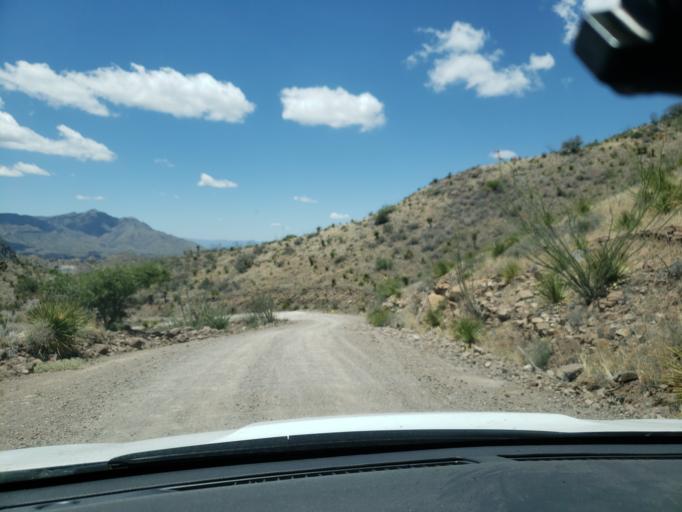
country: MX
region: Chihuahua
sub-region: Ojinaga
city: Manuel Ojinaga
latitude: 30.0399
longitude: -104.4689
